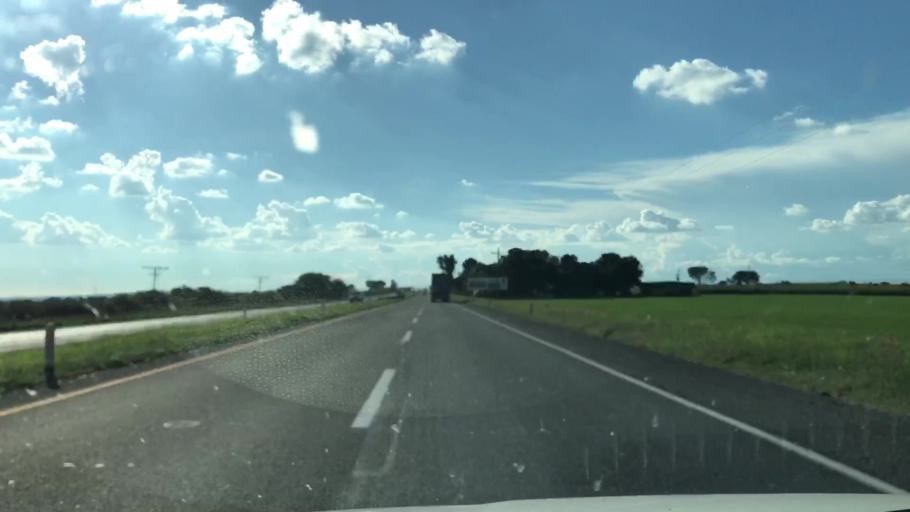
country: MX
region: Jalisco
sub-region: San Juan de los Lagos
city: Mezquitic de la Magdalena
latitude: 21.2896
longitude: -102.2286
